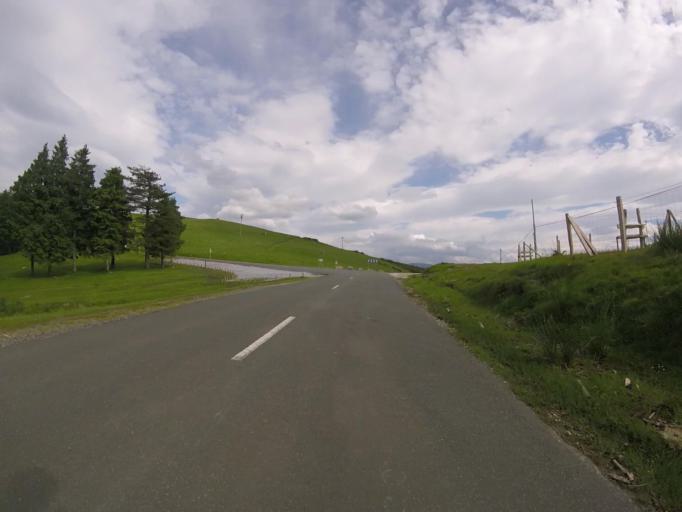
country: ES
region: Navarre
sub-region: Provincia de Navarra
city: Arano
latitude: 43.2423
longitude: -1.8412
